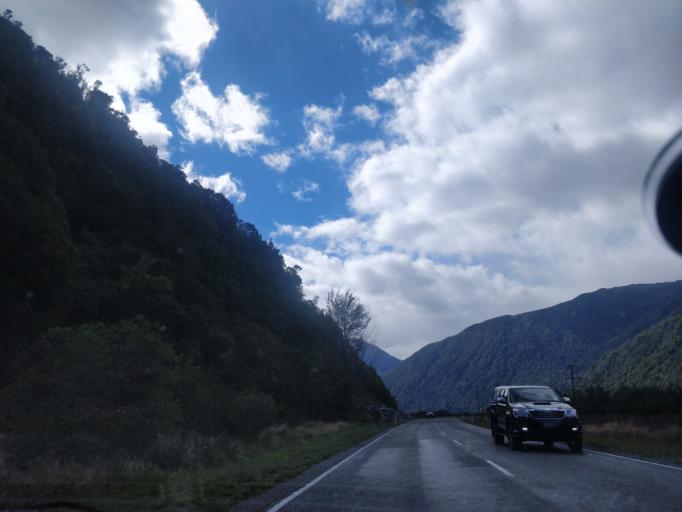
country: NZ
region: West Coast
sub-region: Grey District
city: Greymouth
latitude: -42.7906
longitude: 171.5973
